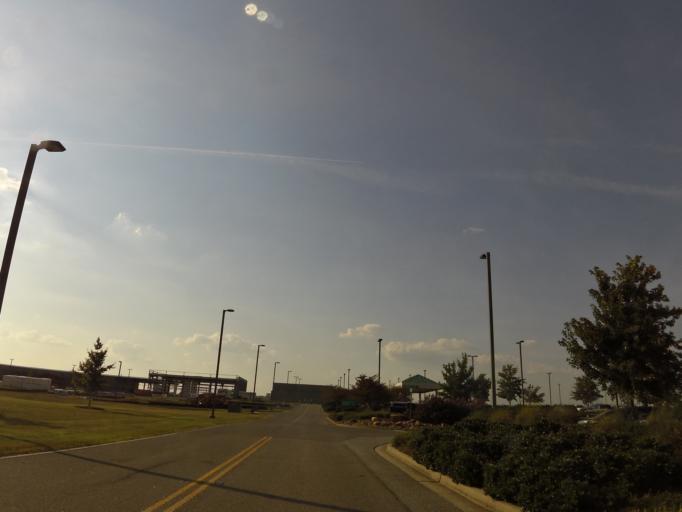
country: US
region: Tennessee
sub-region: Blount County
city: Alcoa
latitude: 35.8030
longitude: -83.9928
